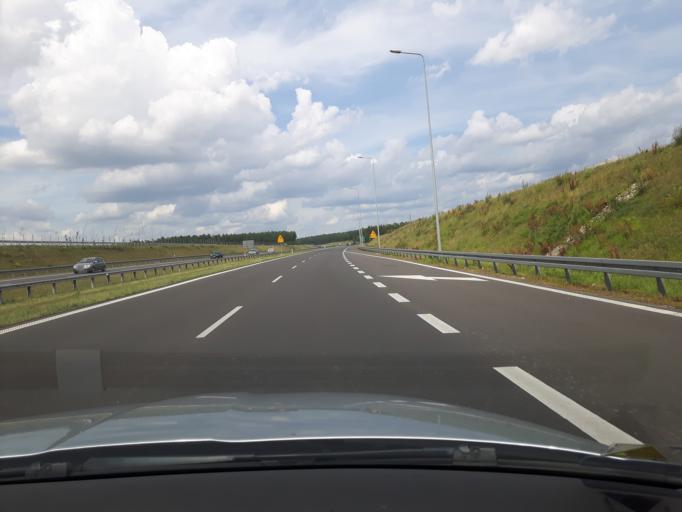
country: PL
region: Masovian Voivodeship
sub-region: Powiat mlawski
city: Wieczfnia Koscielna
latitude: 53.2325
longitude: 20.4200
